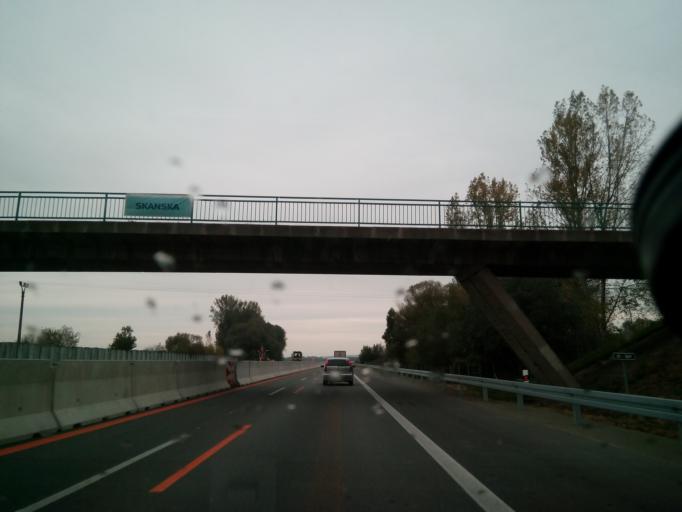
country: SK
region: Kosicky
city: Kosice
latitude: 48.7992
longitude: 21.3114
